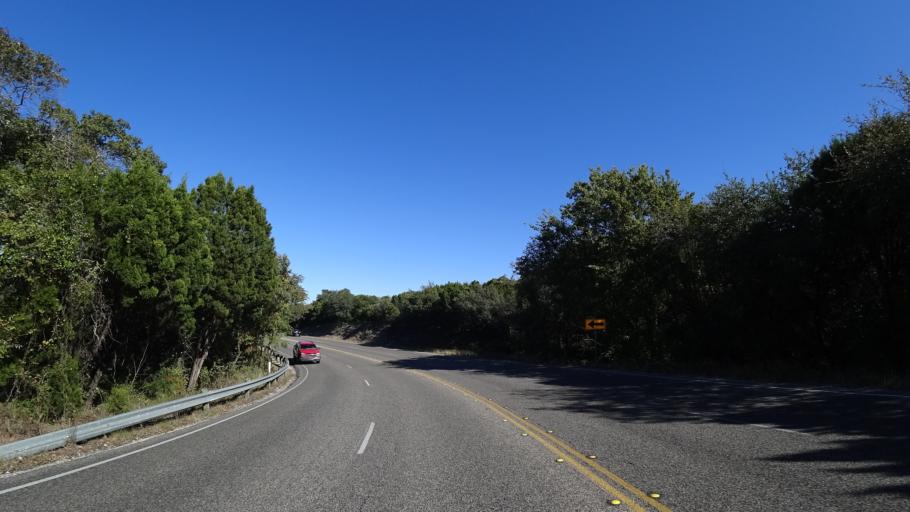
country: US
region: Texas
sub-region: Travis County
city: West Lake Hills
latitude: 30.3463
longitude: -97.7847
